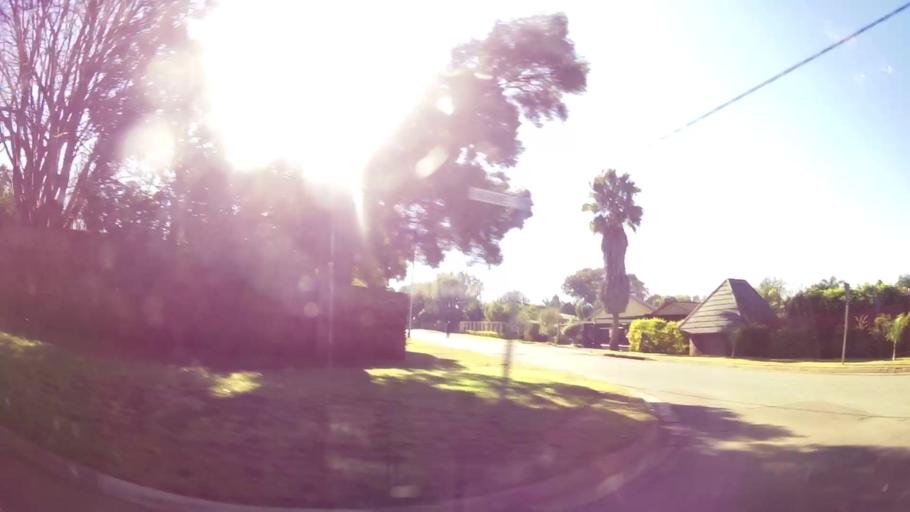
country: ZA
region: Gauteng
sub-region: City of Tshwane Metropolitan Municipality
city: Centurion
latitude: -25.8551
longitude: 28.2048
